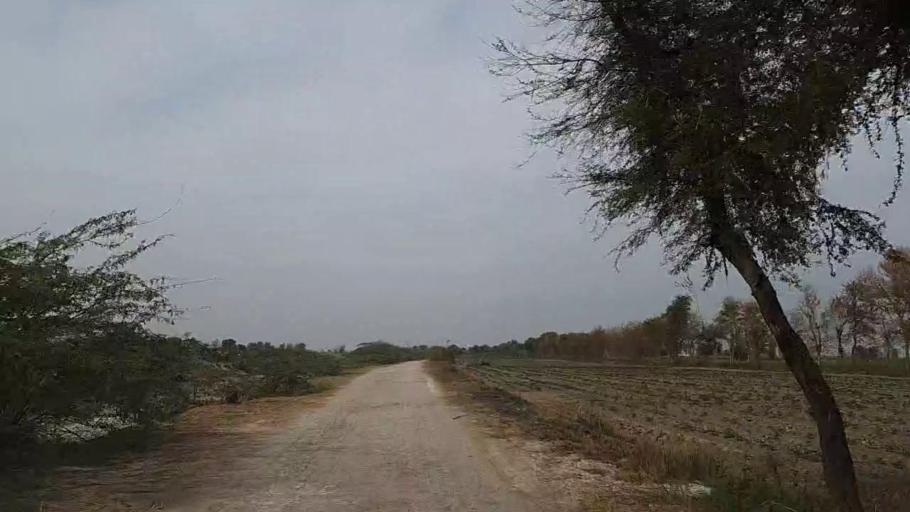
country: PK
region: Sindh
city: Daur
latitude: 26.4204
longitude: 68.4207
